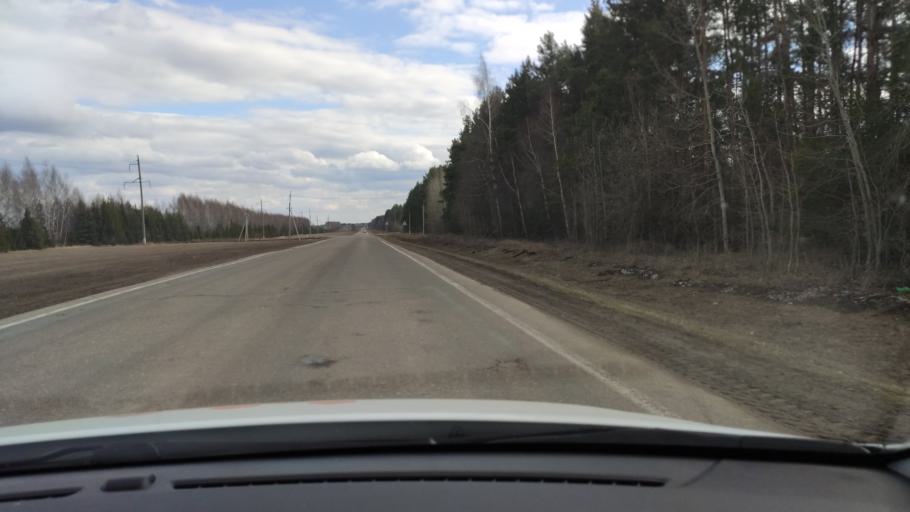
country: RU
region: Tatarstan
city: Vysokaya Gora
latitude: 56.0533
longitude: 49.2112
